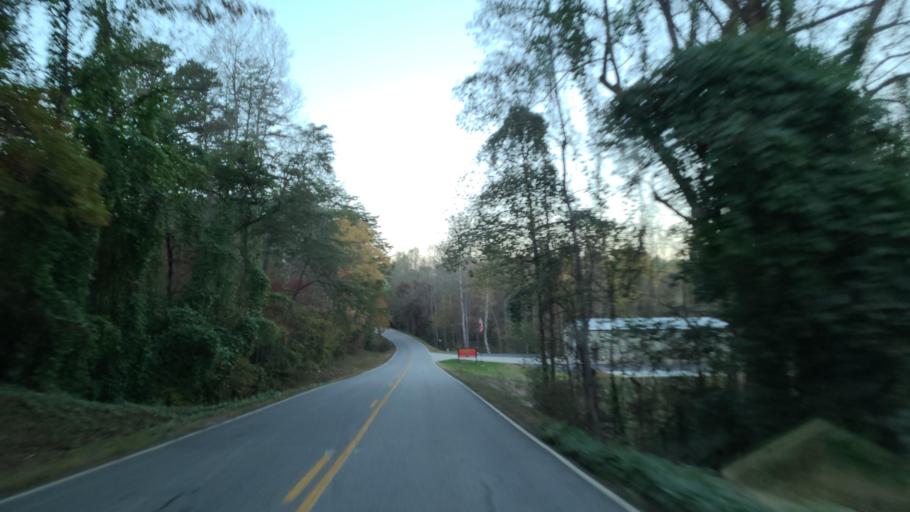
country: US
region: Georgia
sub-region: Towns County
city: Hiawassee
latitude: 34.9474
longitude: -83.8596
